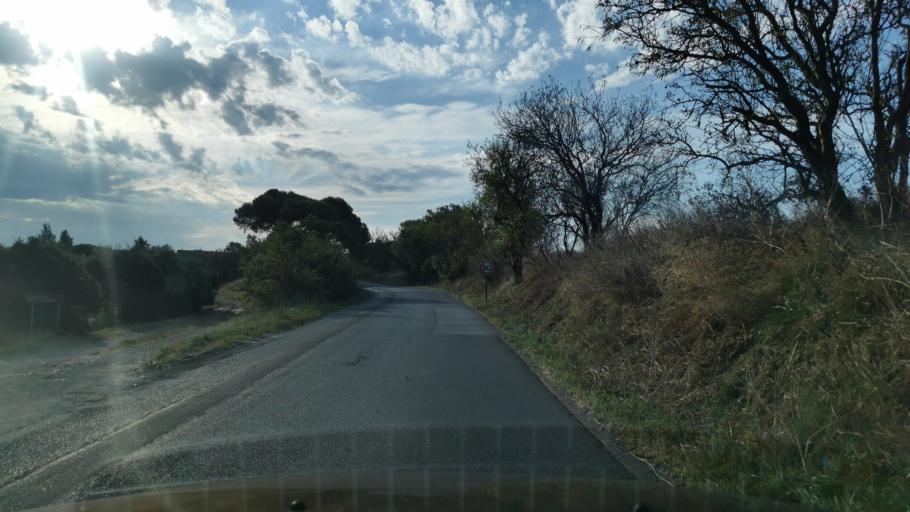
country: FR
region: Languedoc-Roussillon
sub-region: Departement de l'Aude
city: Narbonne
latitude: 43.1441
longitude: 3.0156
